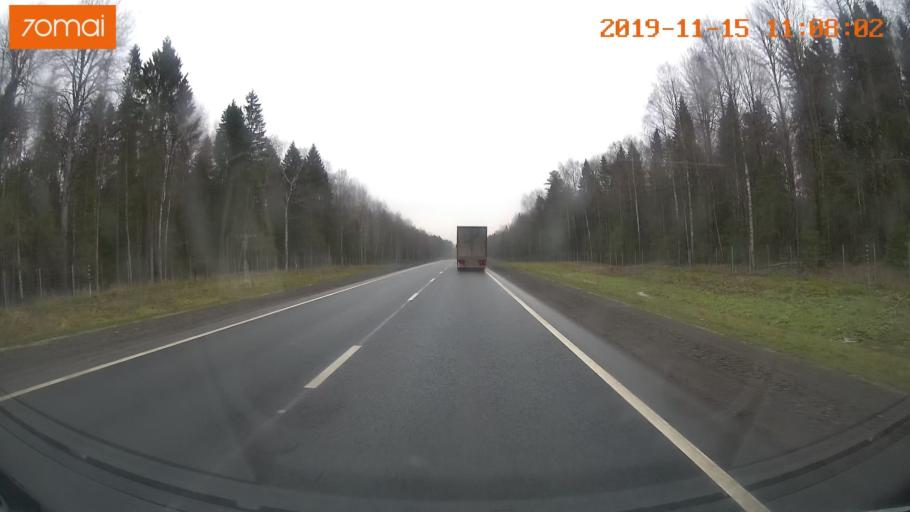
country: RU
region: Vologda
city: Chebsara
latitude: 59.1198
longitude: 39.0642
